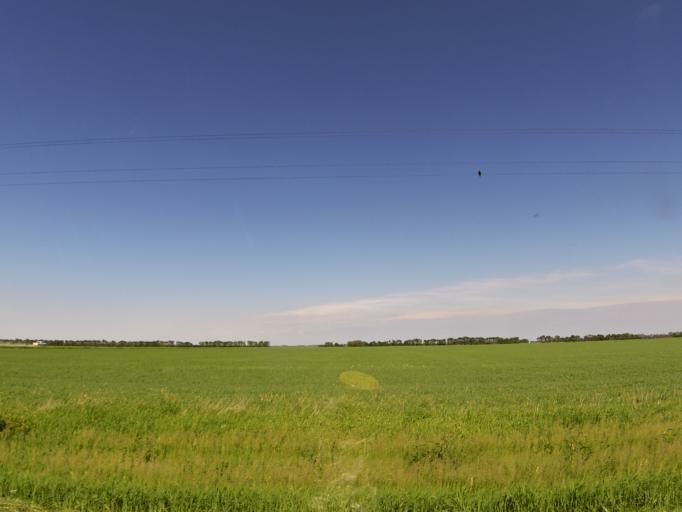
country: US
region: North Dakota
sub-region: Walsh County
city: Grafton
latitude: 48.3233
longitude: -97.2553
